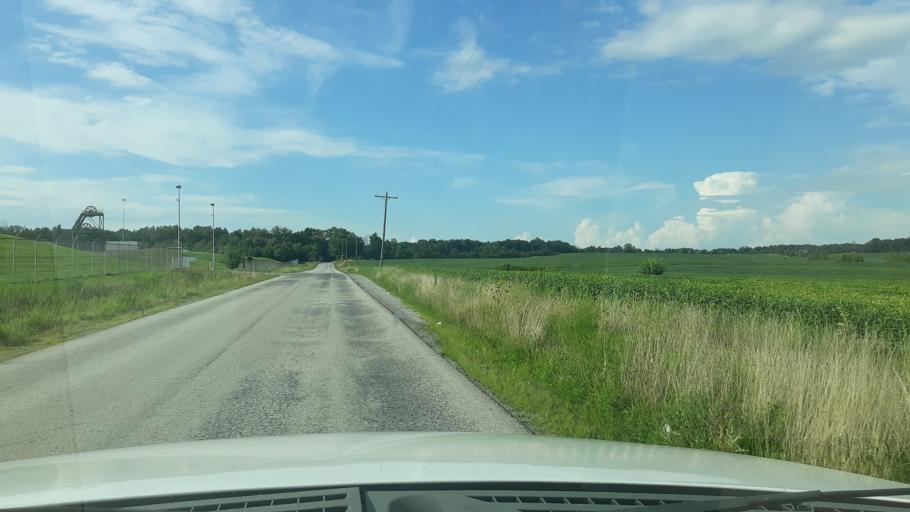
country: US
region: Illinois
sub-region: Saline County
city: Harrisburg
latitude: 37.8369
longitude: -88.5813
